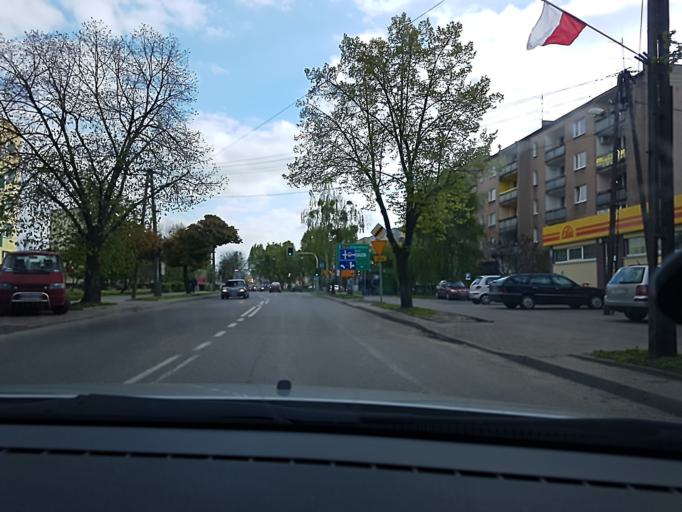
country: PL
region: Masovian Voivodeship
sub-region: Powiat sochaczewski
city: Sochaczew
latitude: 52.2296
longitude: 20.2455
